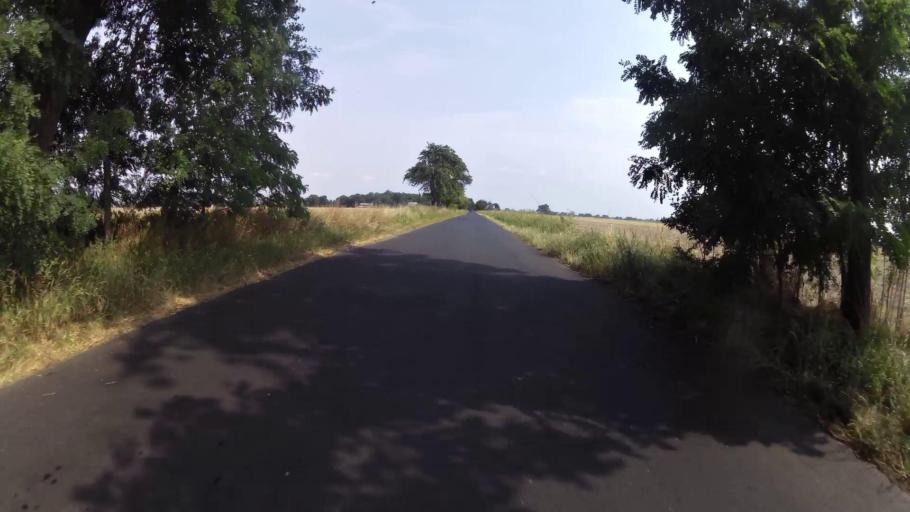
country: PL
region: West Pomeranian Voivodeship
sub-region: Powiat pyrzycki
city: Lipiany
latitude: 52.9718
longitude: 14.9783
